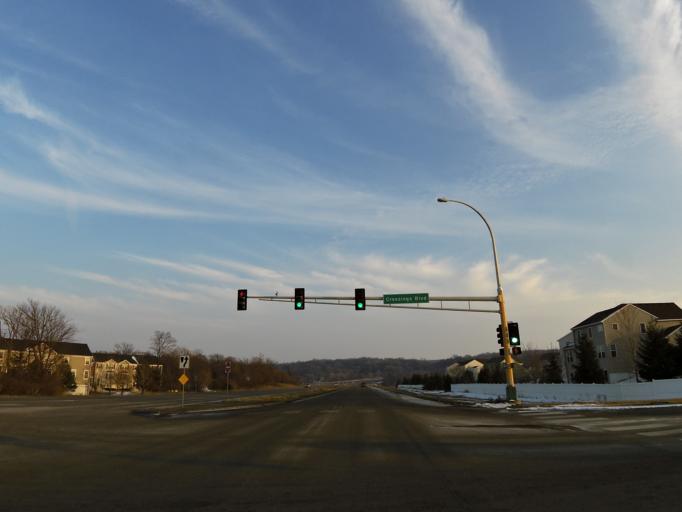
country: US
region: Minnesota
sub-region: Scott County
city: Prior Lake
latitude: 44.7716
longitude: -93.4120
